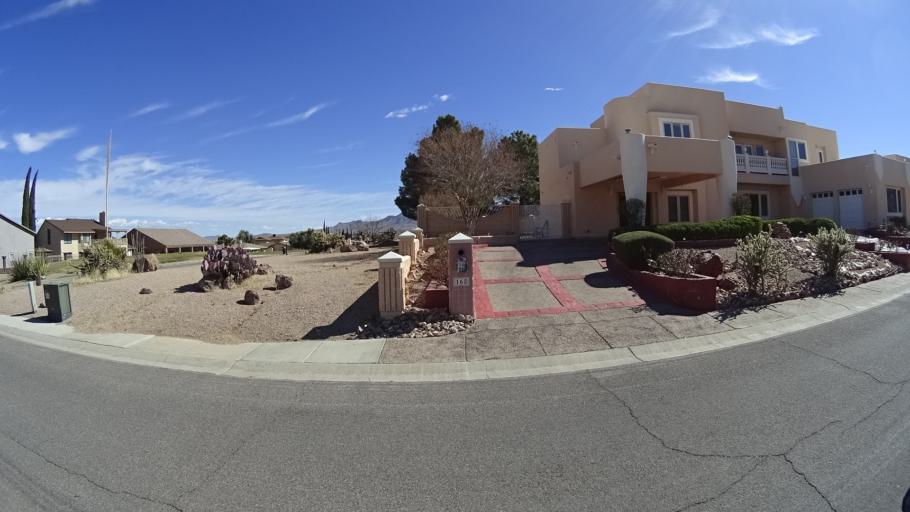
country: US
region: Arizona
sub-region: Mohave County
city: Kingman
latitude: 35.2120
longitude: -114.0454
